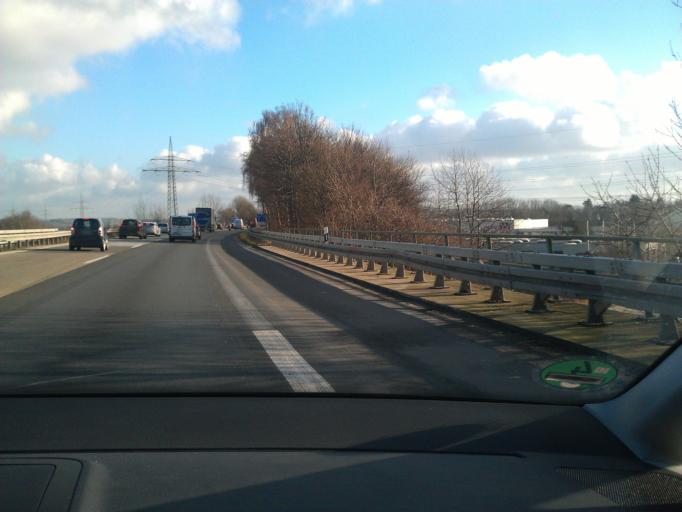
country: DE
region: North Rhine-Westphalia
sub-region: Regierungsbezirk Koln
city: Wurselen
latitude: 50.8039
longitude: 6.1479
